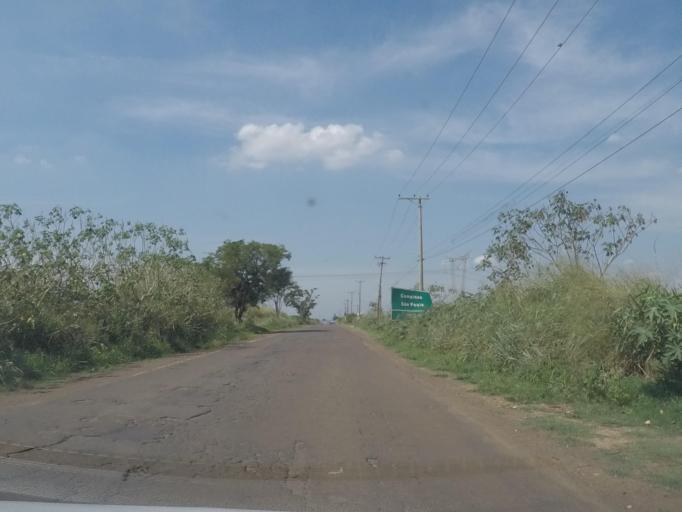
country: BR
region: Sao Paulo
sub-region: Sumare
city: Sumare
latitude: -22.8661
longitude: -47.2957
